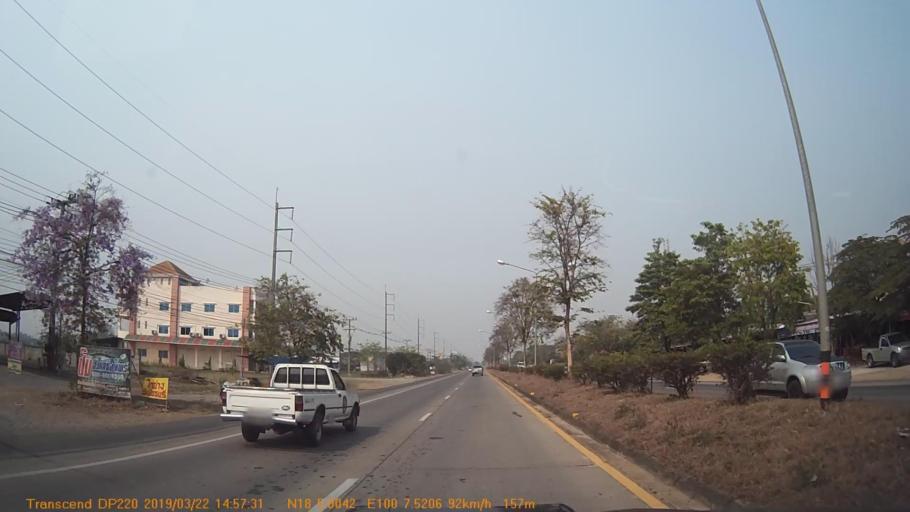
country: TH
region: Phrae
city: Sung Men
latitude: 18.0837
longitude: 100.1255
